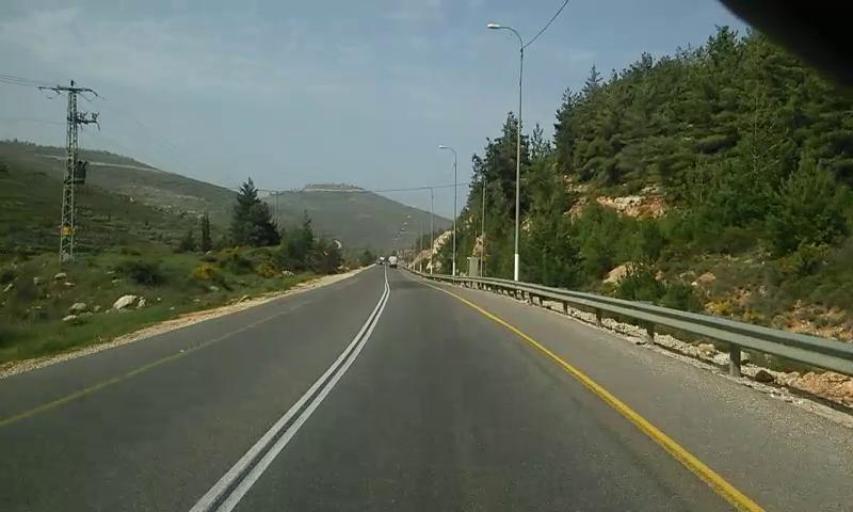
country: PS
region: West Bank
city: As Sawiyah
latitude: 32.0637
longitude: 35.2645
